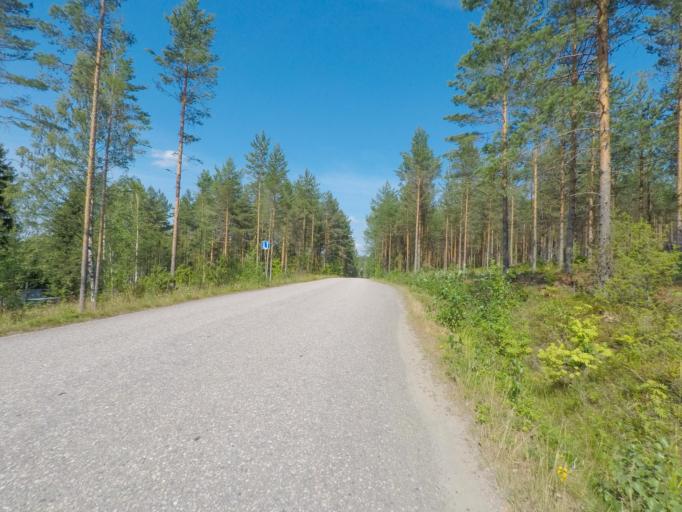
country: FI
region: Southern Savonia
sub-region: Mikkeli
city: Puumala
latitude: 61.4169
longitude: 28.0925
